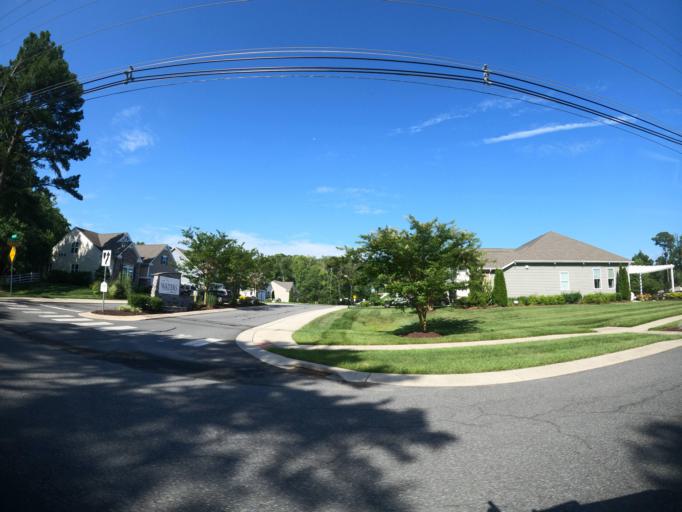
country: US
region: Delaware
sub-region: Sussex County
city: Ocean View
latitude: 38.4815
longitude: -75.1185
